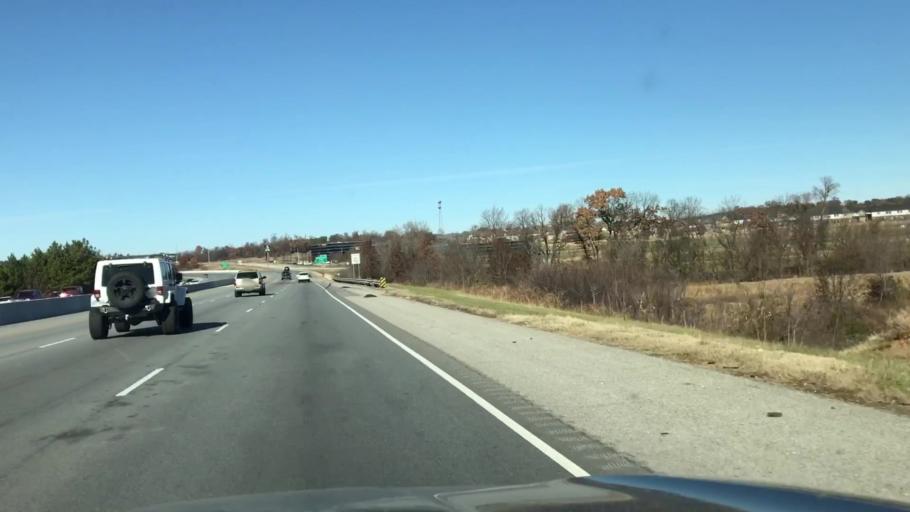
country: US
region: Arkansas
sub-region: Benton County
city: Lowell
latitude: 36.2911
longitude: -94.1620
